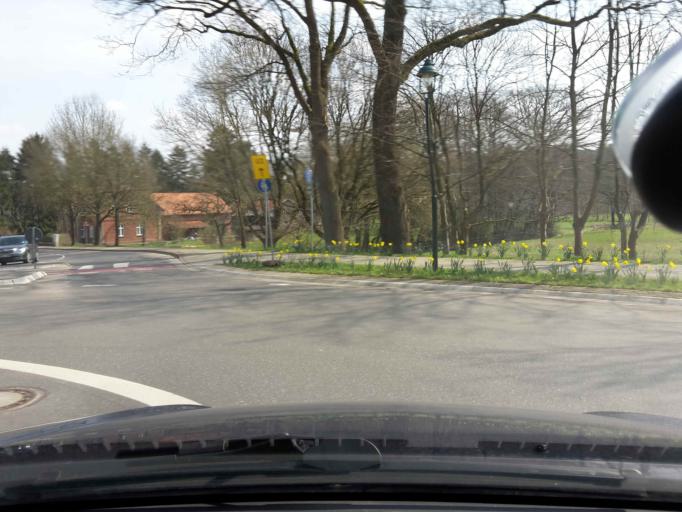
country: DE
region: Lower Saxony
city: Jesteburg
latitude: 53.2889
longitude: 9.9153
